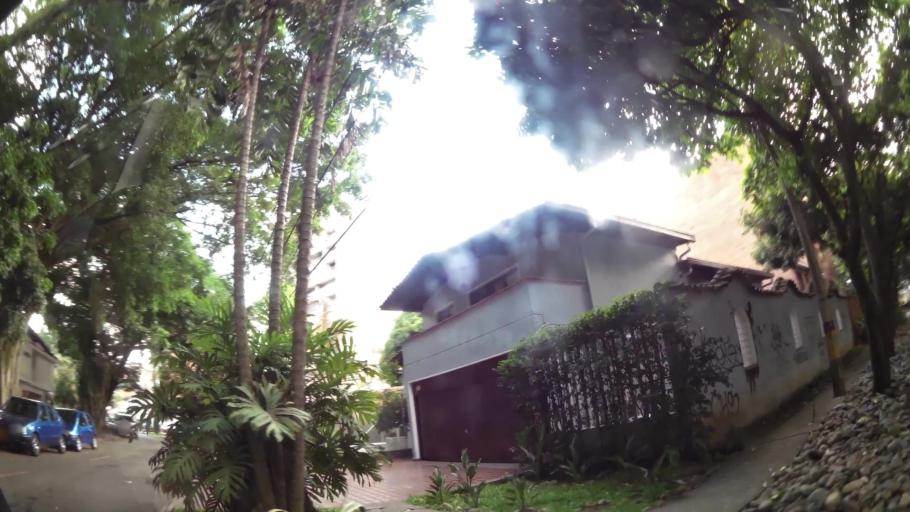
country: CO
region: Antioquia
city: Itagui
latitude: 6.2110
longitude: -75.5752
